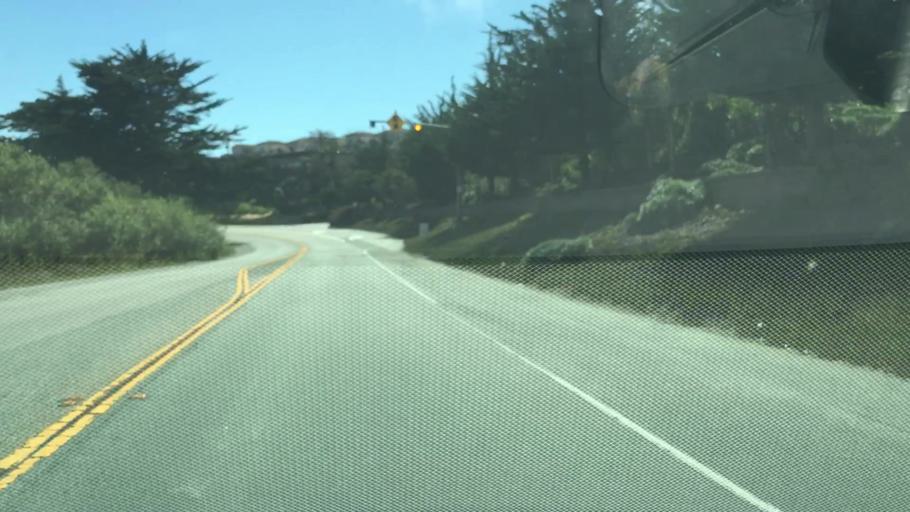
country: US
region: California
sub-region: San Mateo County
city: Colma
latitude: 37.6487
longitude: -122.4720
